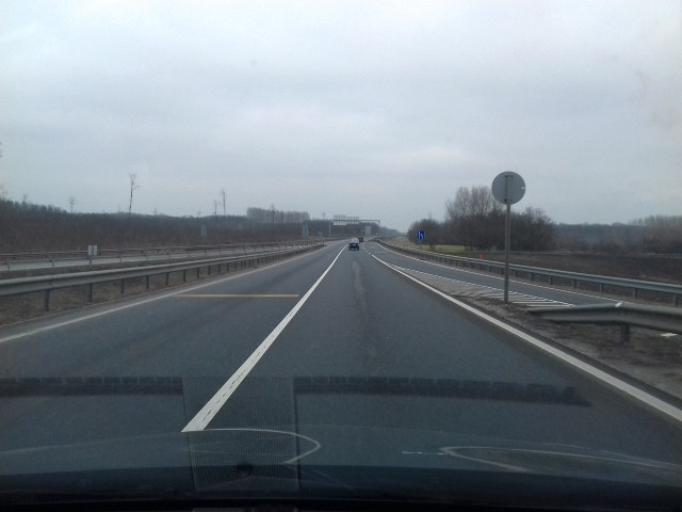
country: HU
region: Szabolcs-Szatmar-Bereg
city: Nagykallo
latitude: 47.8998
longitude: 21.8175
